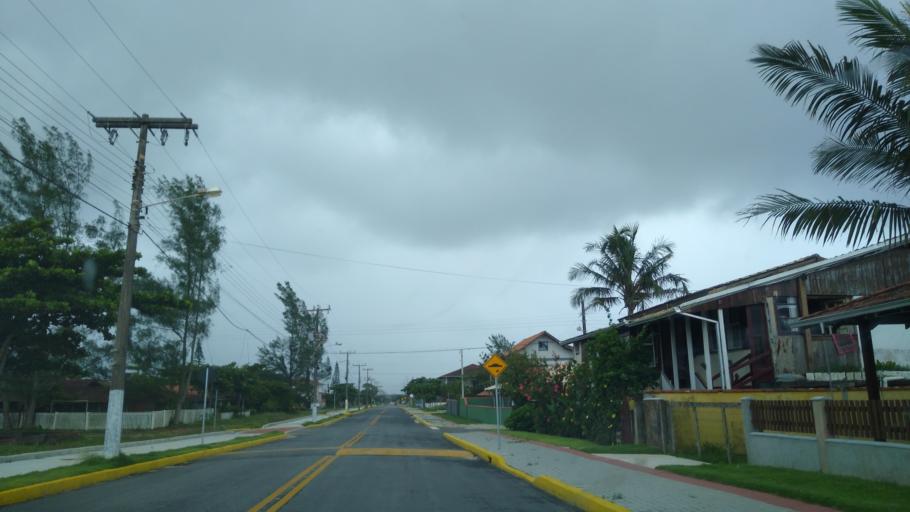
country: BR
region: Santa Catarina
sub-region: Sao Francisco Do Sul
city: Sao Francisco do Sul
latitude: -26.2384
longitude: -48.5070
